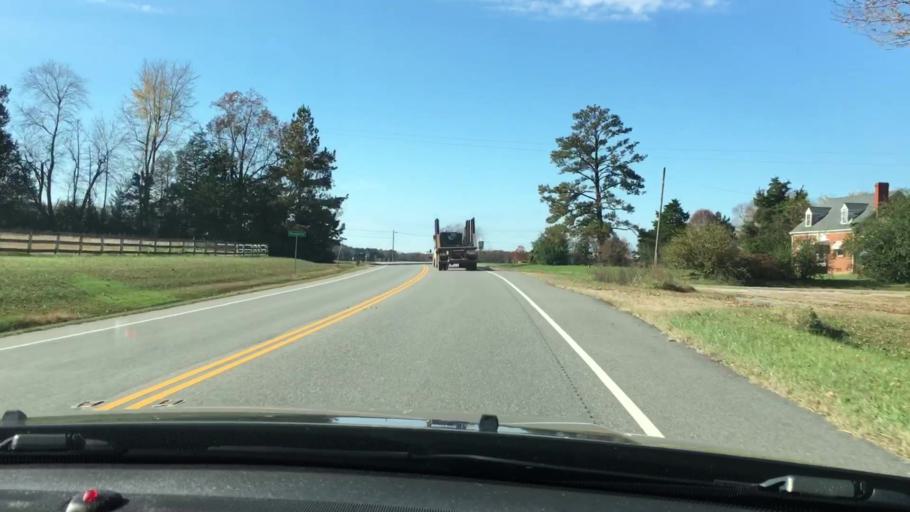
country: US
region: Virginia
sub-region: Hanover County
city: Hanover
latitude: 37.8092
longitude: -77.2704
